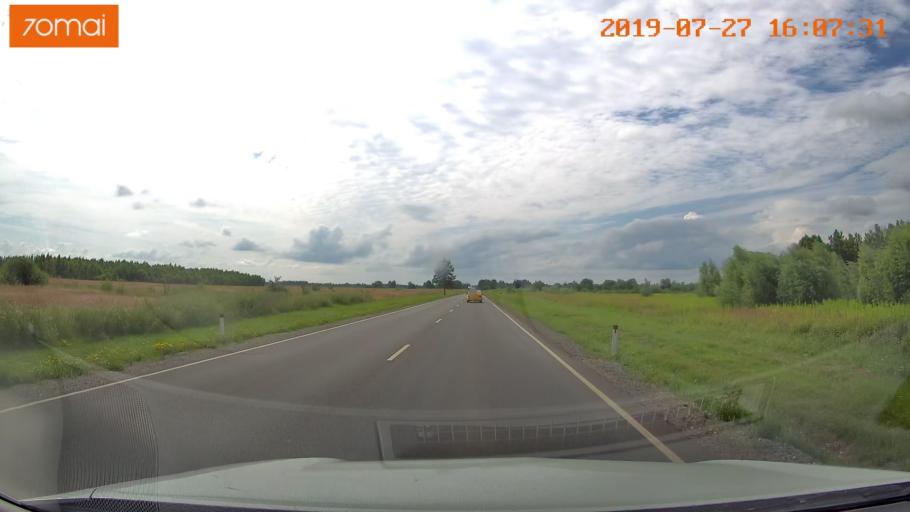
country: RU
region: Kaliningrad
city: Chernyakhovsk
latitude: 54.6354
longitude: 21.7557
